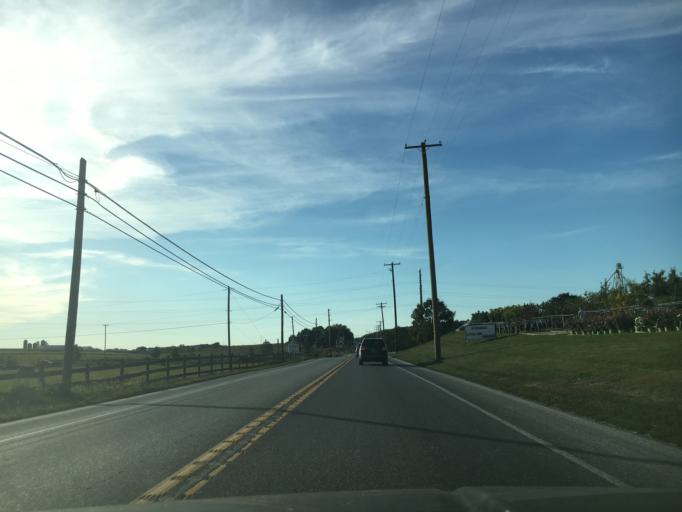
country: US
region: Pennsylvania
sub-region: Lancaster County
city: Ephrata
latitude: 40.1560
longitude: -76.1319
